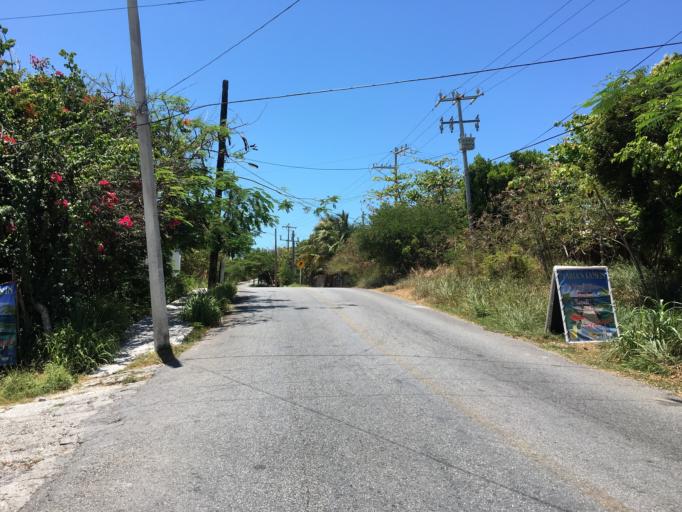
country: MX
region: Quintana Roo
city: Isla Mujeres
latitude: 21.2113
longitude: -86.7215
